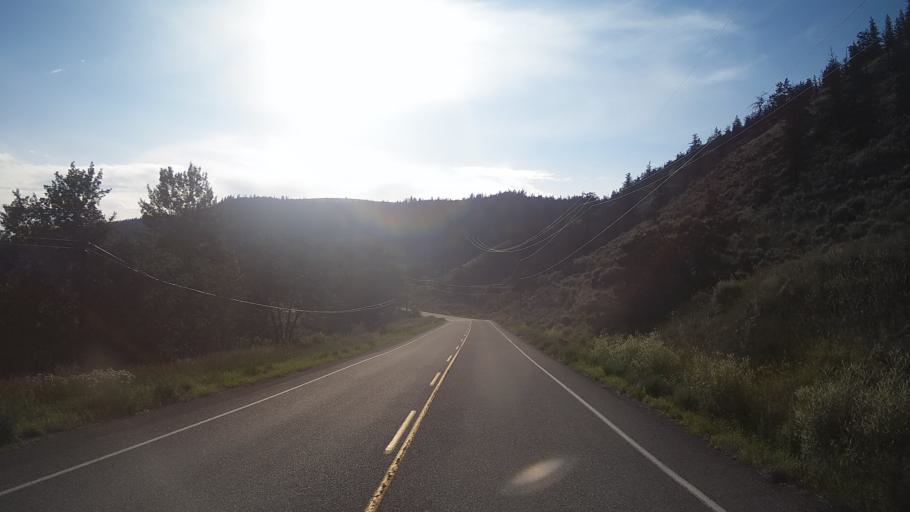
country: CA
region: British Columbia
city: Lillooet
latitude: 50.8978
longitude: -121.7745
